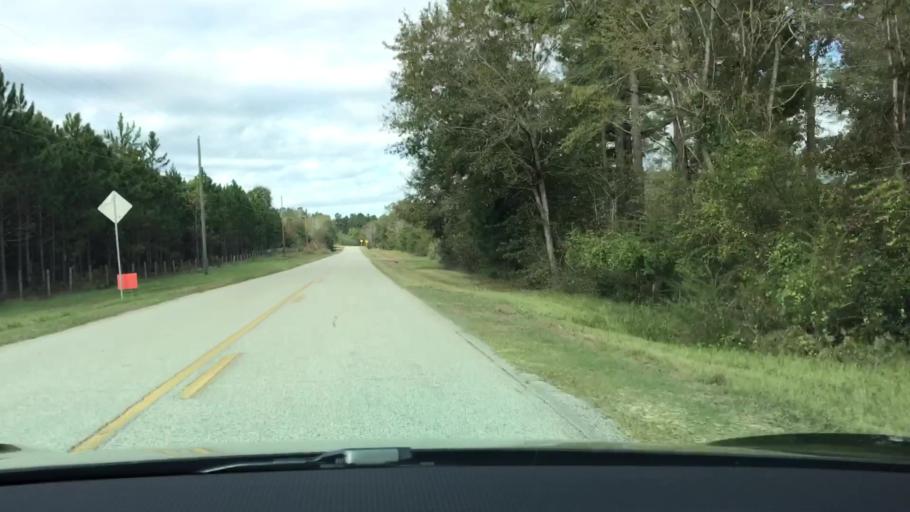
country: US
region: Georgia
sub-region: Jefferson County
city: Wadley
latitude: 32.7998
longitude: -82.3810
